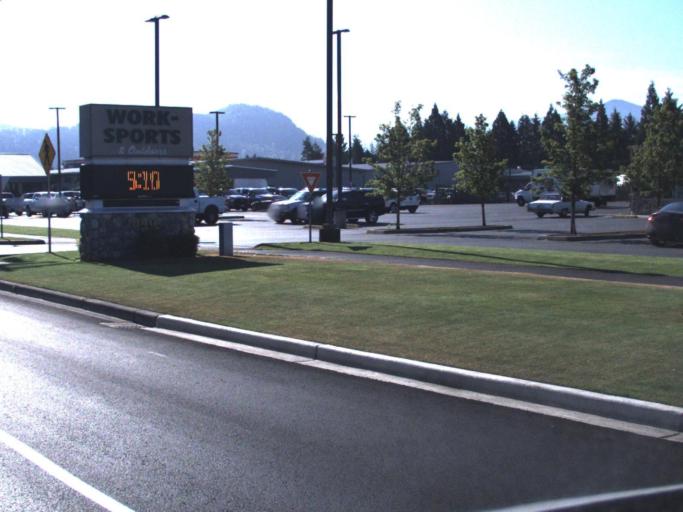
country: US
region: Washington
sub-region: King County
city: Enumclaw
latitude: 47.1994
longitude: -121.9892
